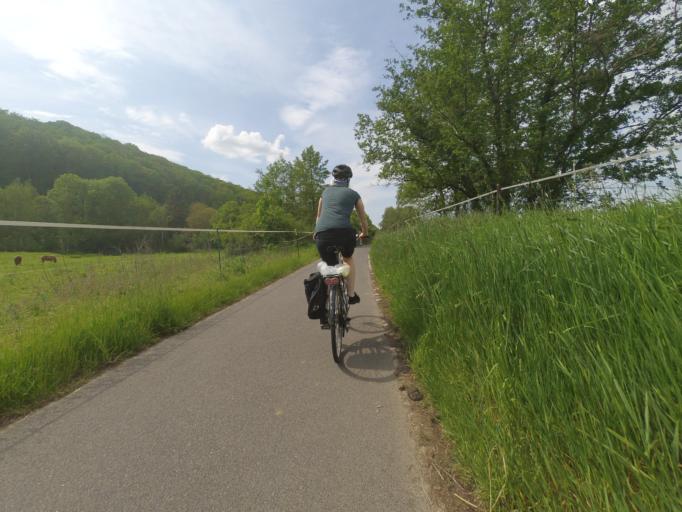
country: DE
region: Saxony
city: Klipphausen
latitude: 51.1229
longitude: 13.5377
